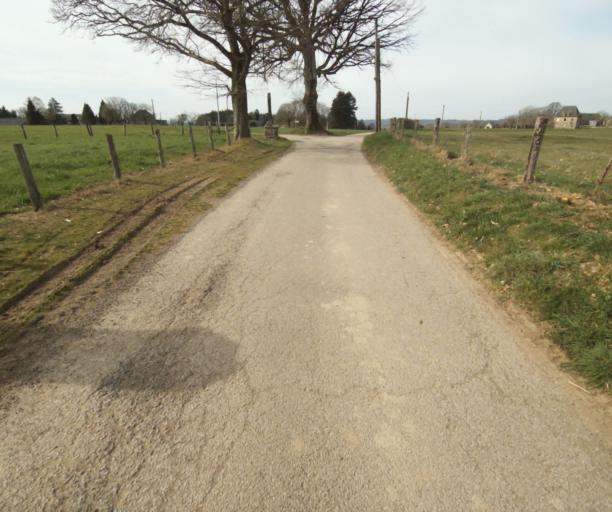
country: FR
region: Limousin
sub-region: Departement de la Correze
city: Correze
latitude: 45.4178
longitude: 1.8207
